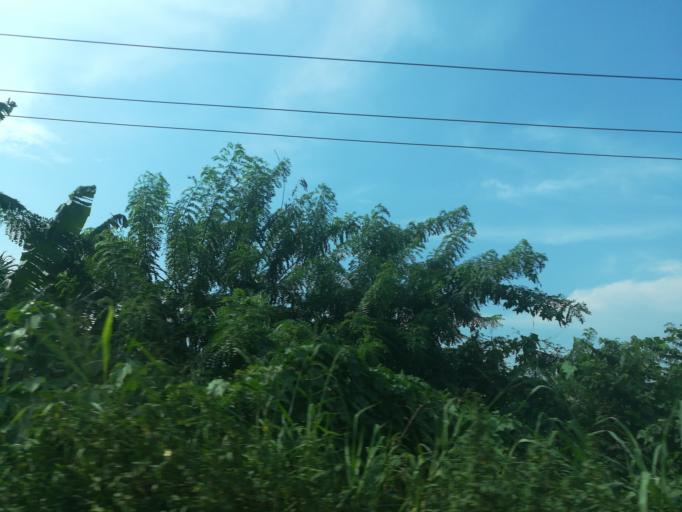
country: NG
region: Lagos
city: Ikorodu
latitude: 6.6303
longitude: 3.5167
